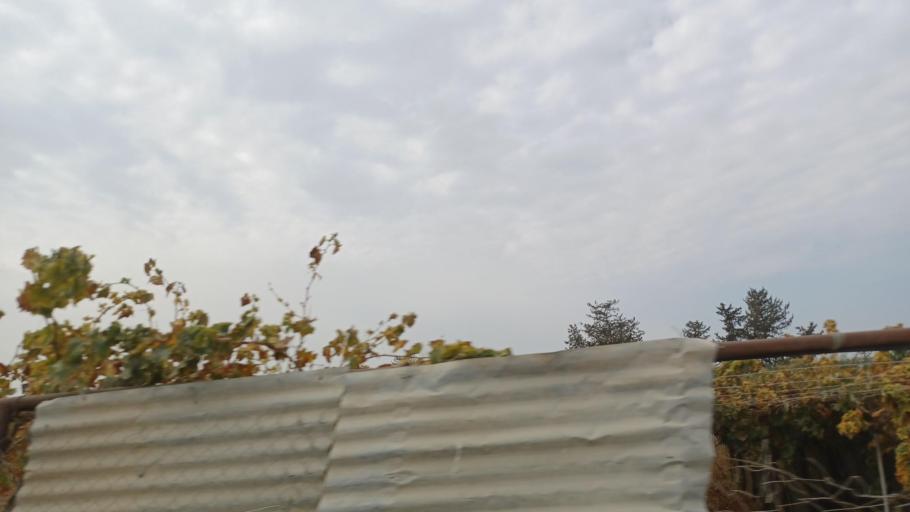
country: CY
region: Larnaka
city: Kolossi
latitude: 34.6675
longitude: 32.9502
